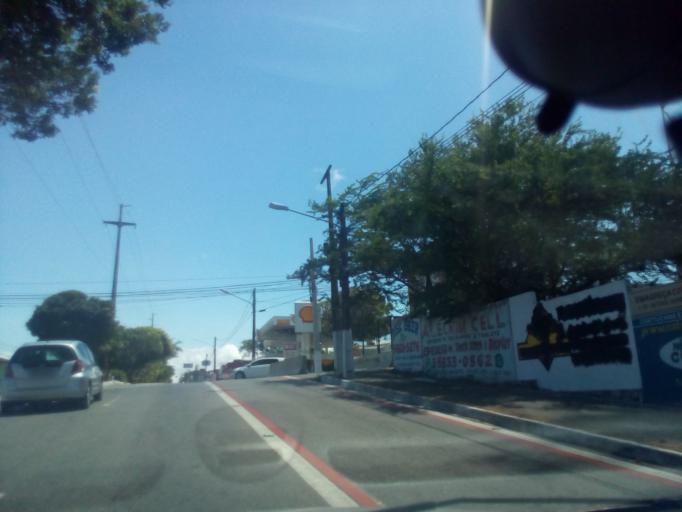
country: BR
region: Rio Grande do Norte
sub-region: Natal
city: Natal
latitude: -5.8315
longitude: -35.2174
